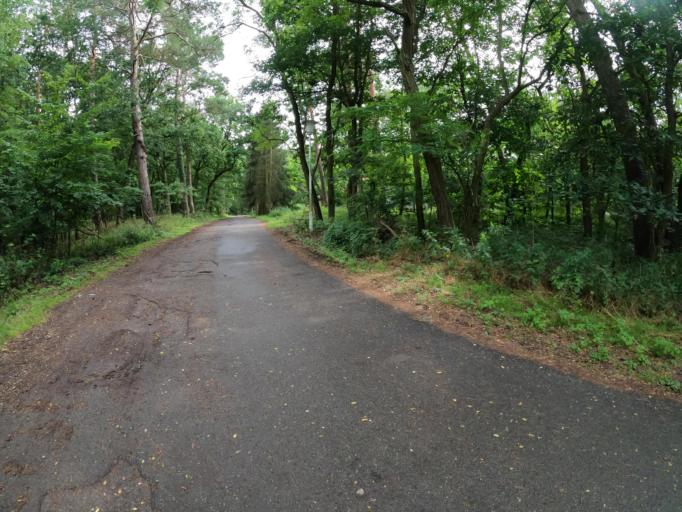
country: DE
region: Brandenburg
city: Angermunde
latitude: 53.0269
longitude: 13.9094
